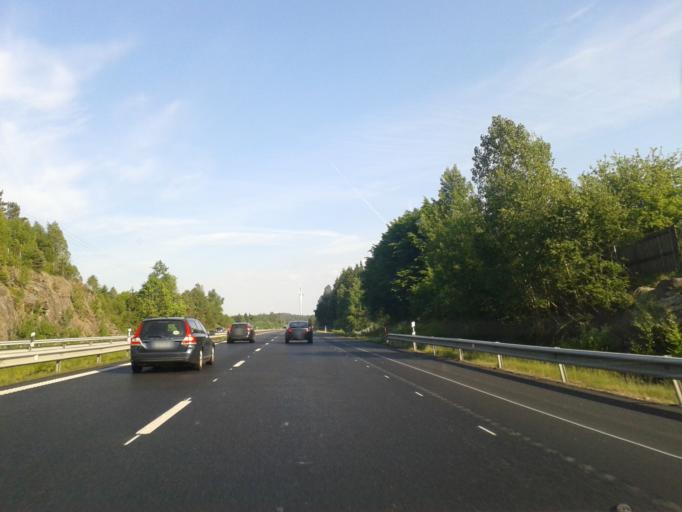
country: SE
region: Vaestra Goetaland
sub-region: Kungalvs Kommun
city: Kode
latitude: 57.9098
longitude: 11.8969
